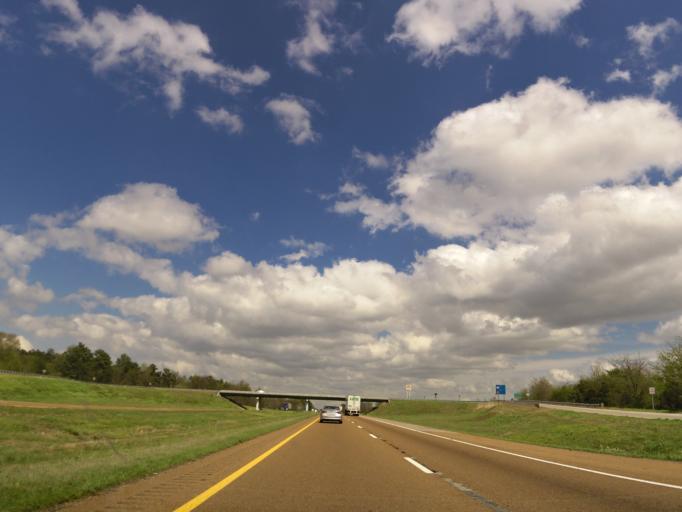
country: US
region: Tennessee
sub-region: Tipton County
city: Mason
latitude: 35.3477
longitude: -89.5210
